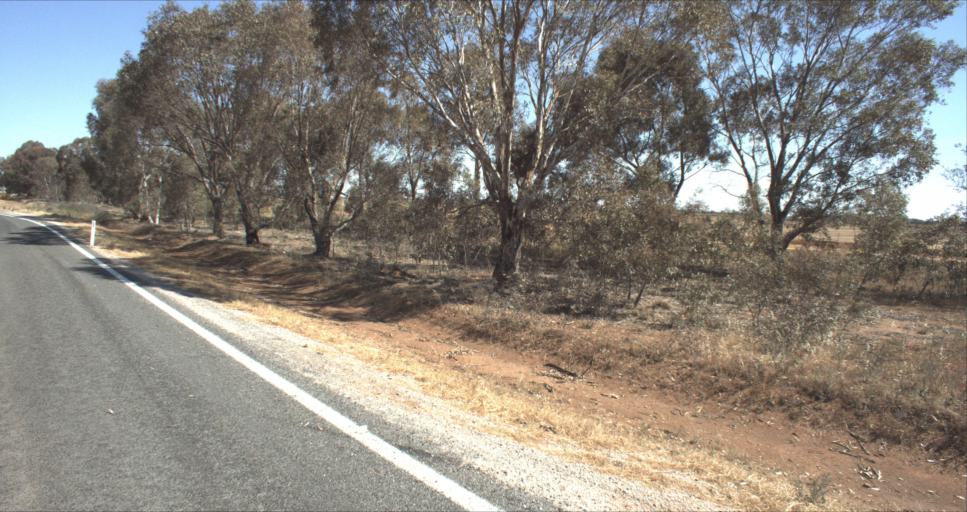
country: AU
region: New South Wales
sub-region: Leeton
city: Leeton
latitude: -34.4938
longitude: 146.4322
